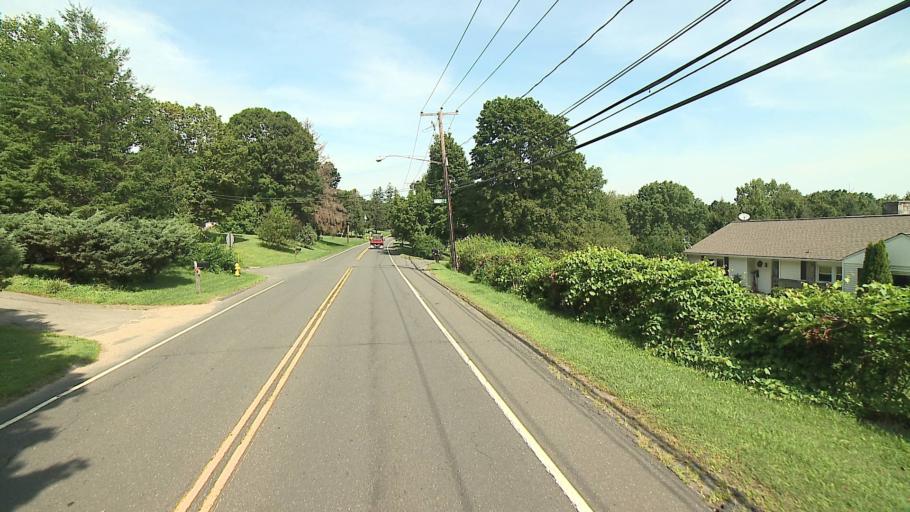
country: US
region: Connecticut
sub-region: Fairfield County
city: Danbury
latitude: 41.4267
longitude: -73.4840
